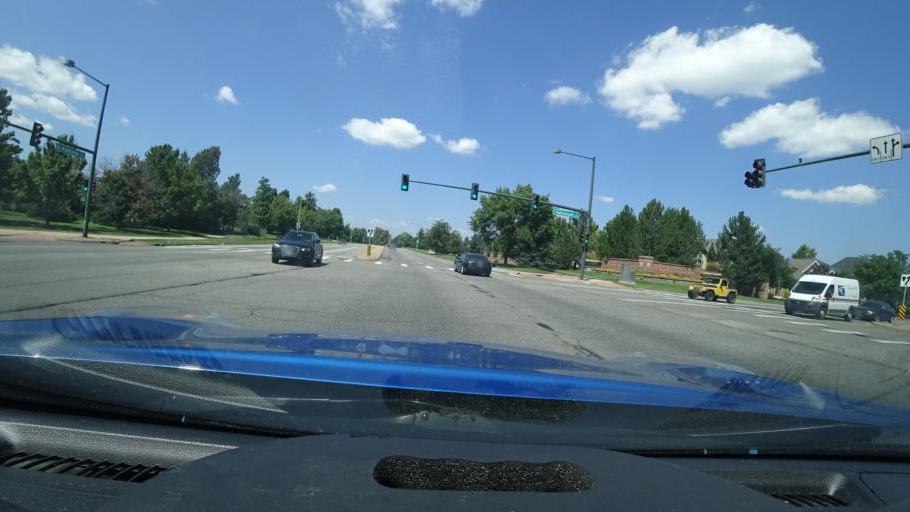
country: US
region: Colorado
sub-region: Arapahoe County
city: Glendale
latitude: 39.7112
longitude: -104.8926
